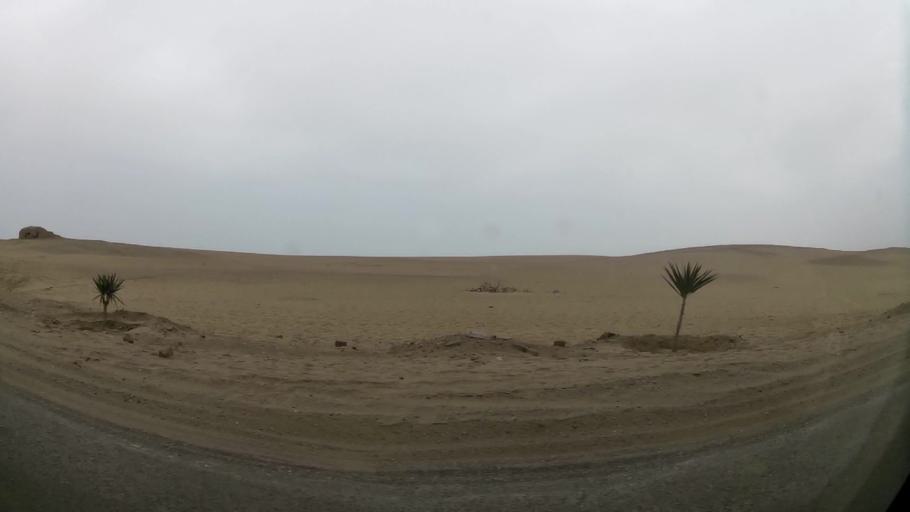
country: PE
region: Lima
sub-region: Lima
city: Punta Hermosa
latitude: -12.2473
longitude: -76.9074
